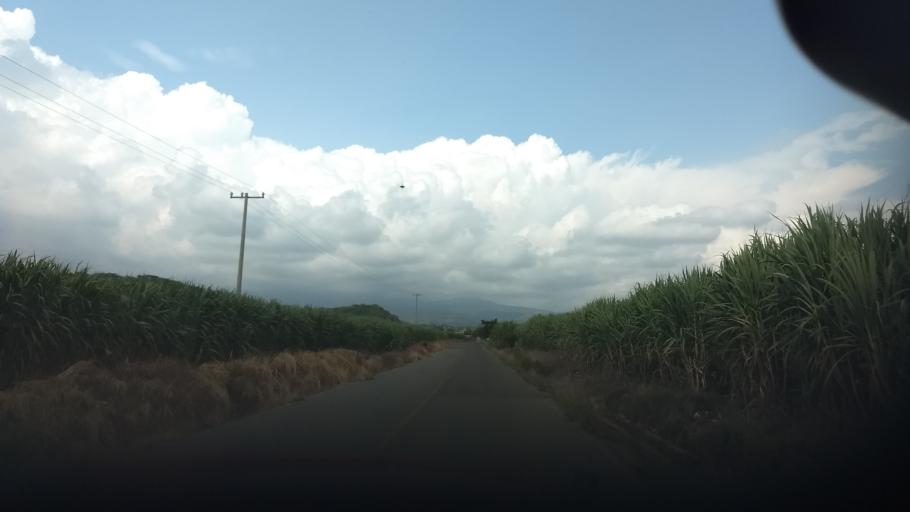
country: MX
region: Jalisco
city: Tonila
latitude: 19.4163
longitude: -103.4883
